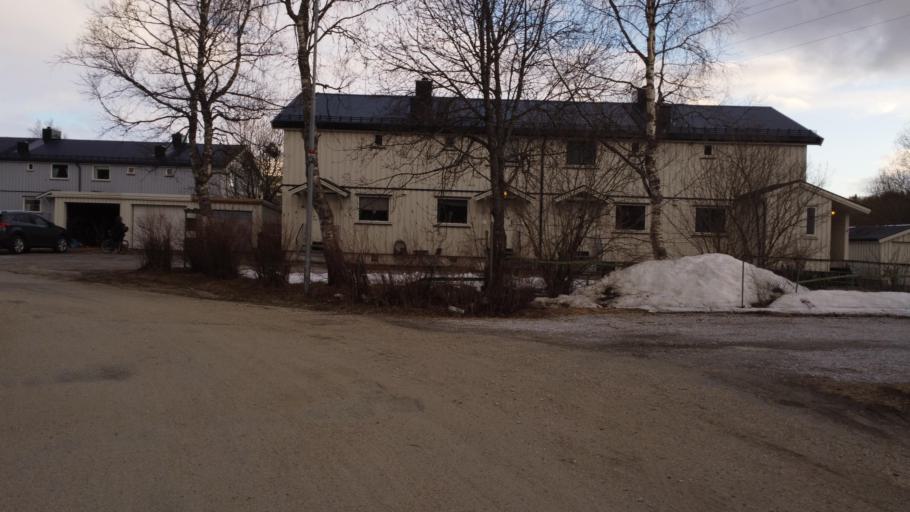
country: NO
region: Nordland
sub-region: Rana
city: Mo i Rana
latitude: 66.3264
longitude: 14.1687
